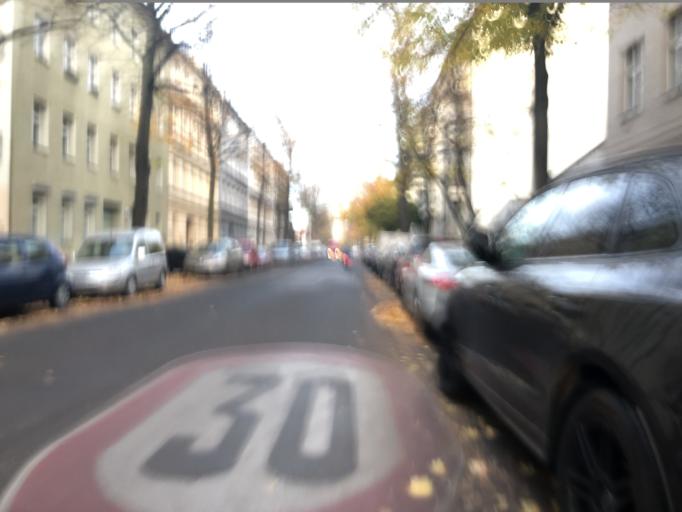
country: DE
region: Berlin
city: Weissensee
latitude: 52.5477
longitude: 13.4468
